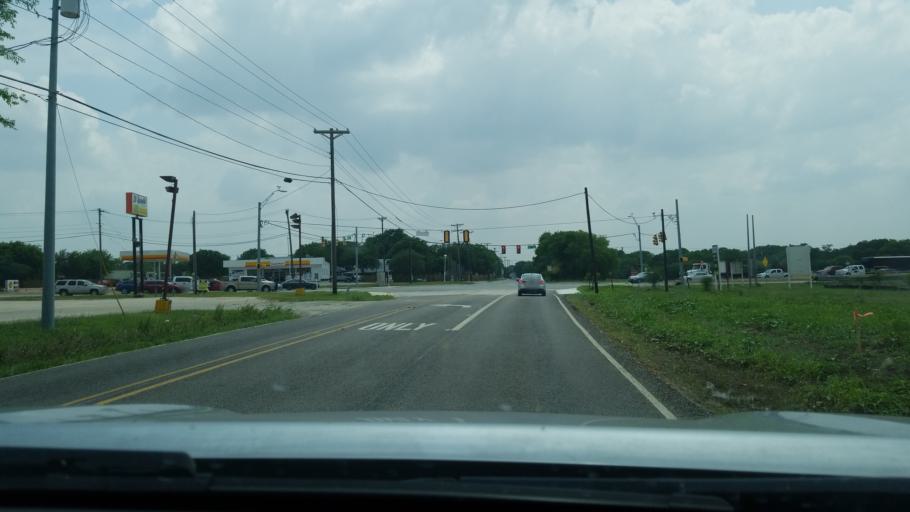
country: US
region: Texas
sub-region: Comal County
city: New Braunfels
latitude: 29.7447
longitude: -98.0970
